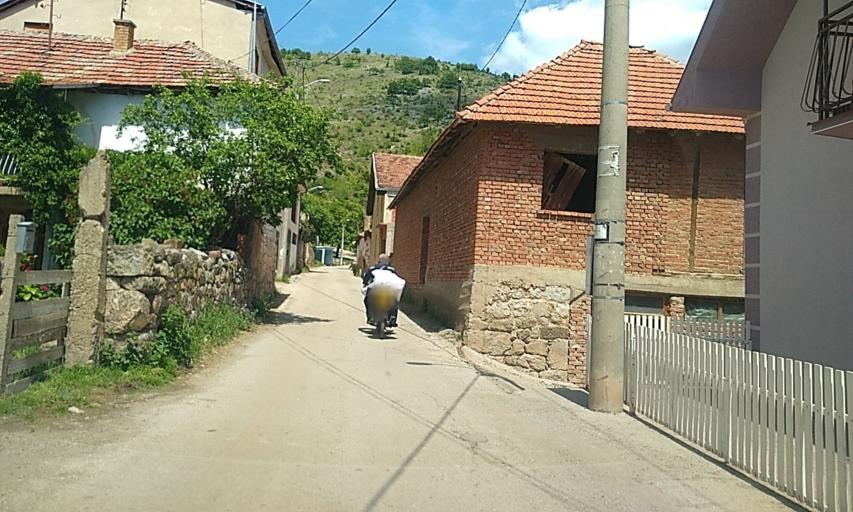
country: RS
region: Central Serbia
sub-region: Nisavski Okrug
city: Niska Banja
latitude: 43.3663
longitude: 21.9996
